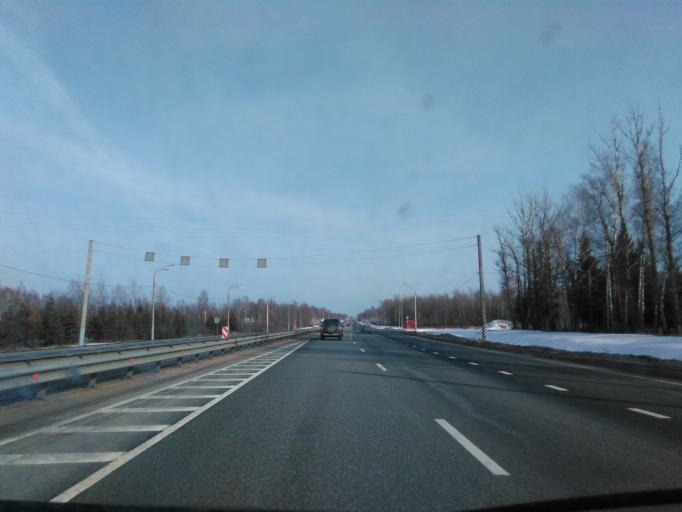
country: RU
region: Smolensk
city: Verkhnedneprovskiy
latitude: 55.1817
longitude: 33.5670
